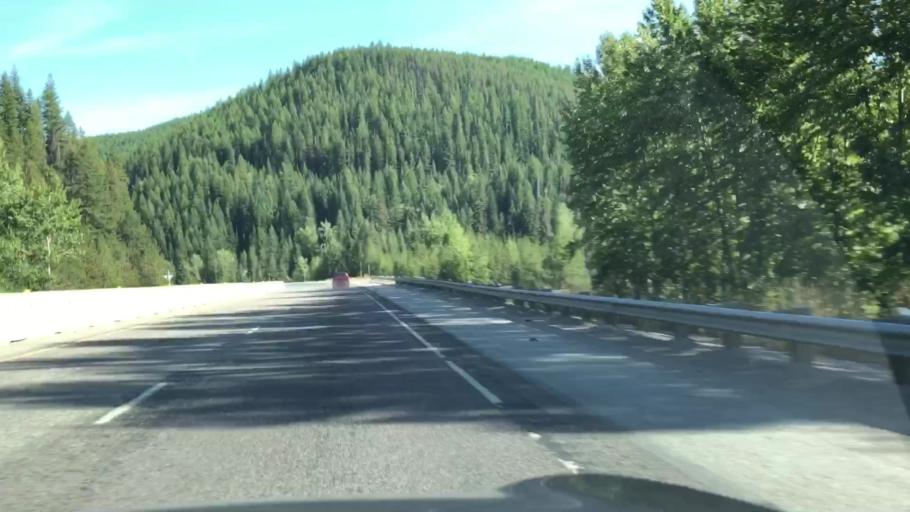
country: US
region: Montana
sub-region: Sanders County
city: Thompson Falls
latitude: 47.4173
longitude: -115.5899
